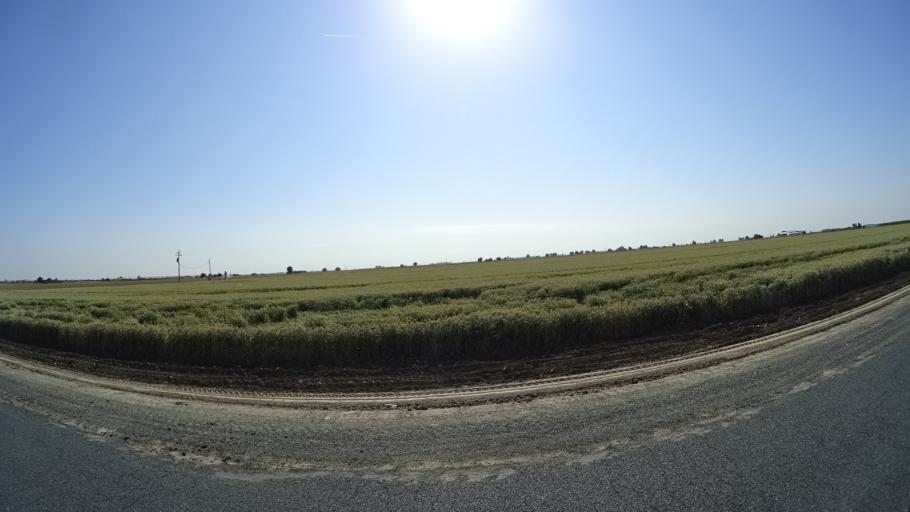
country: US
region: California
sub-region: Kings County
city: Home Garden
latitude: 36.2325
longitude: -119.5831
